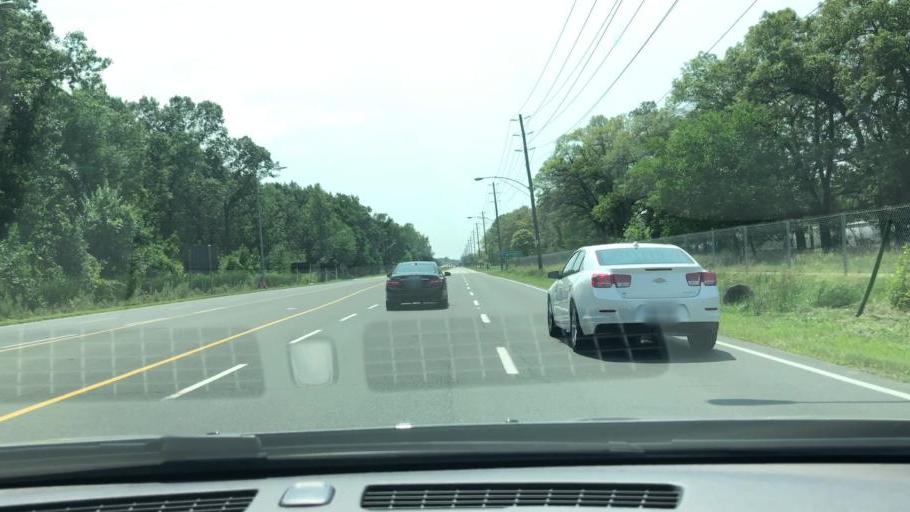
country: US
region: Michigan
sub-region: Wayne County
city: River Rouge
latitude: 42.2694
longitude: -83.0816
